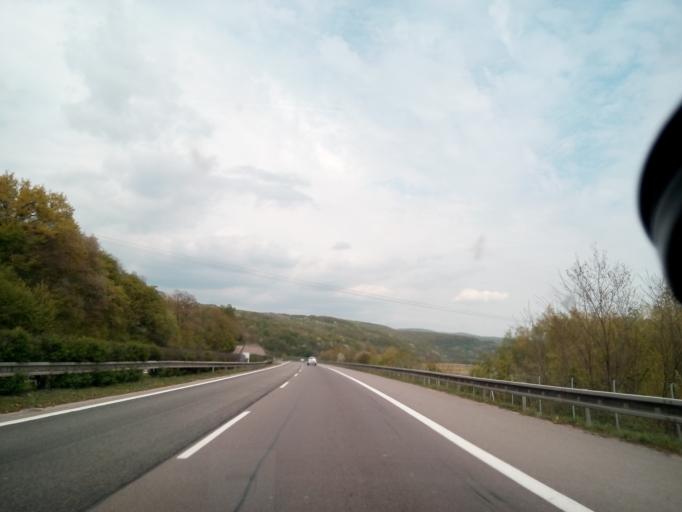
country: SK
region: Trenciansky
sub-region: Okres Trencin
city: Trencin
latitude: 48.8858
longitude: 17.9817
